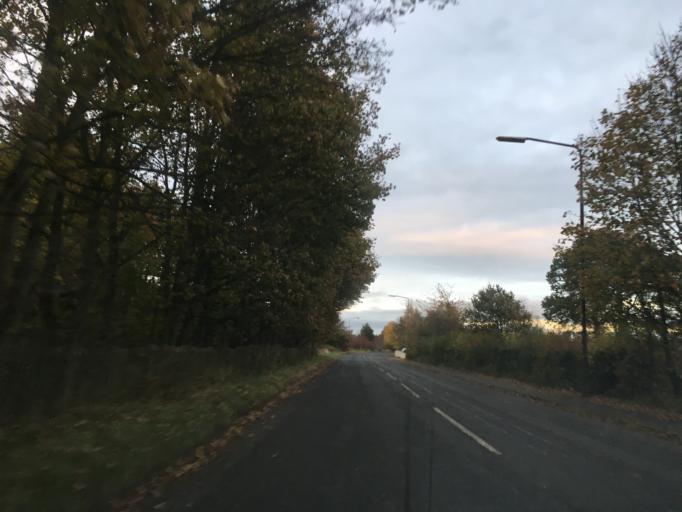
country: GB
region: Scotland
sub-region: Midlothian
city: Loanhead
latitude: 55.8695
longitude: -3.1888
